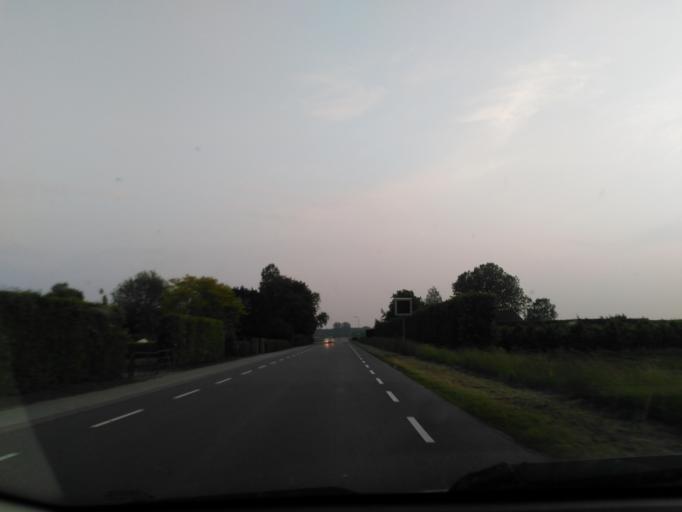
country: BE
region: Flanders
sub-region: Provincie Oost-Vlaanderen
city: Sint-Gillis-Waas
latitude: 51.2811
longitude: 4.1253
